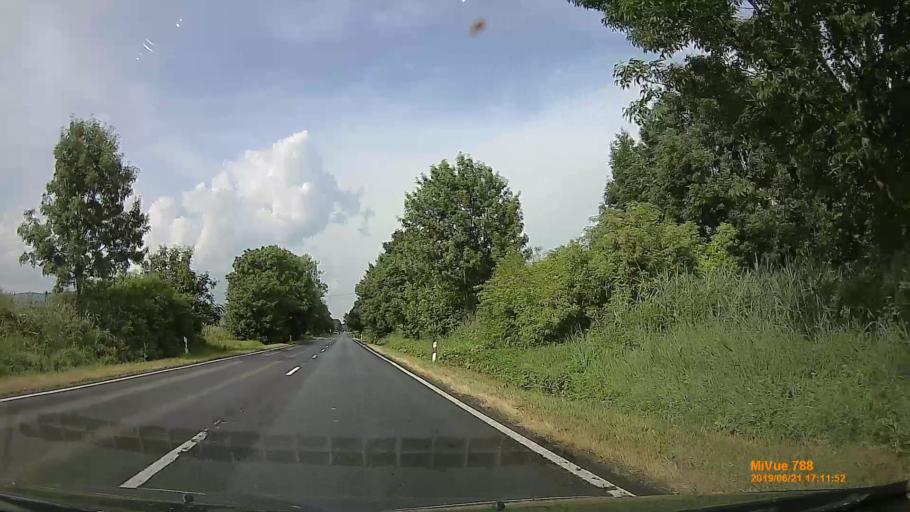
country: HU
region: Baranya
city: Hosszuheteny
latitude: 46.1214
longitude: 18.3645
